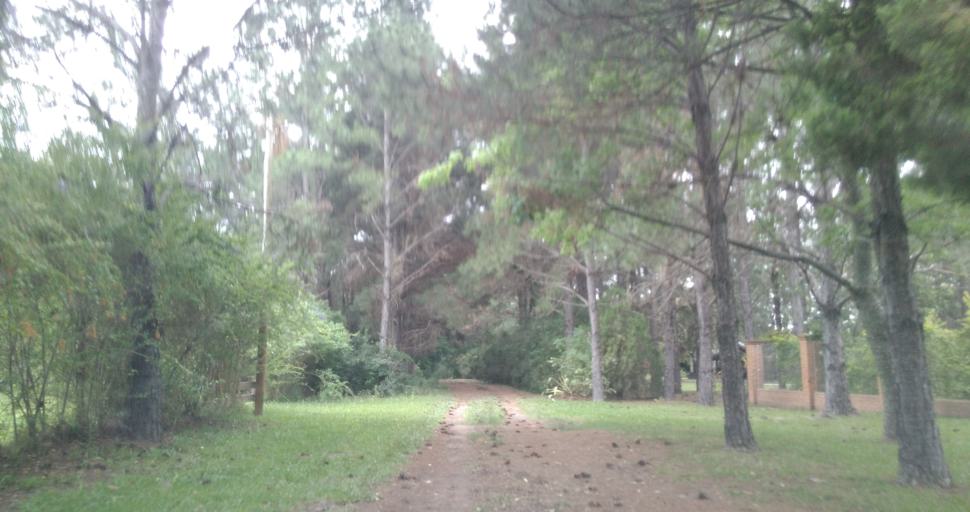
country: AR
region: Chaco
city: Fontana
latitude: -27.4034
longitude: -59.0106
